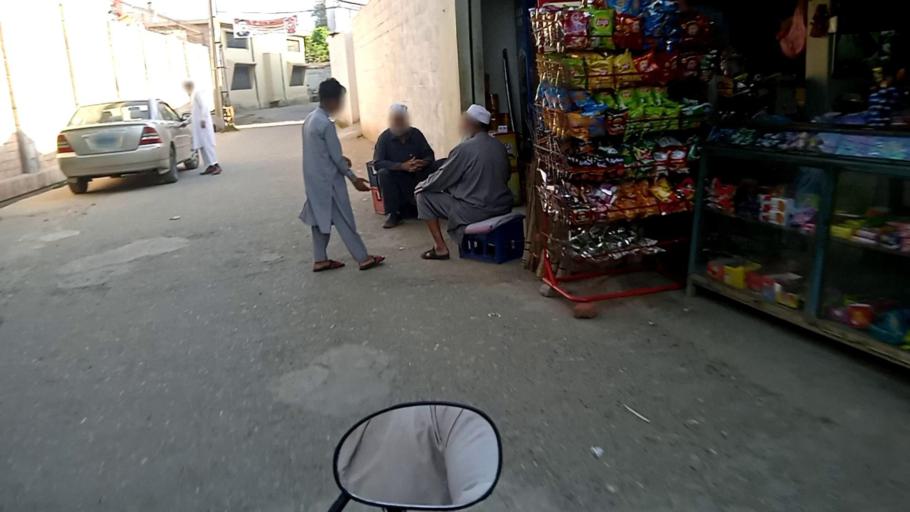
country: PK
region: Khyber Pakhtunkhwa
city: Mingora
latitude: 34.8095
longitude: 72.3611
